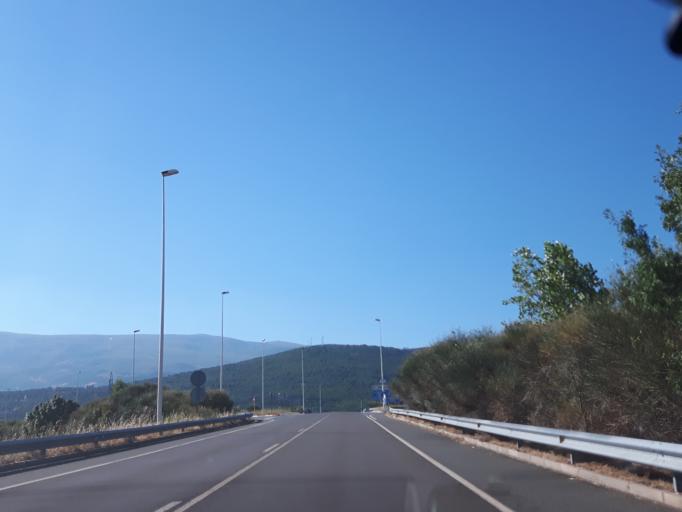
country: ES
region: Castille and Leon
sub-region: Provincia de Salamanca
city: Bejar
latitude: 40.3953
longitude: -5.7837
